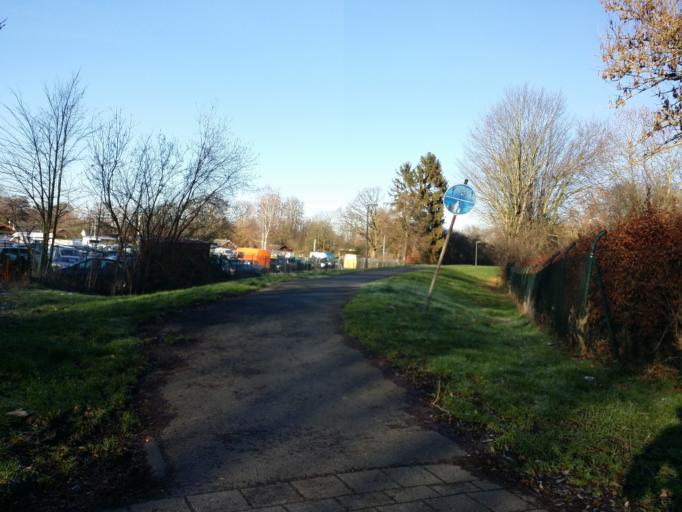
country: DE
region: Lower Saxony
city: Stuhr
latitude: 53.0702
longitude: 8.7625
